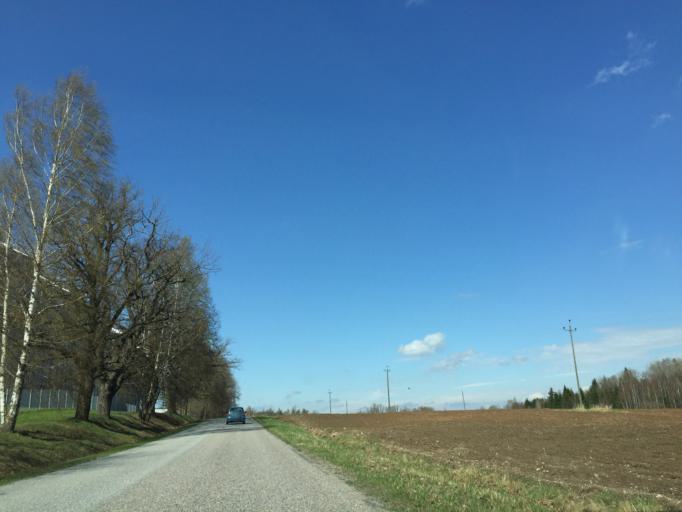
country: EE
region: Tartu
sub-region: Elva linn
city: Elva
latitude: 58.1474
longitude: 26.2336
